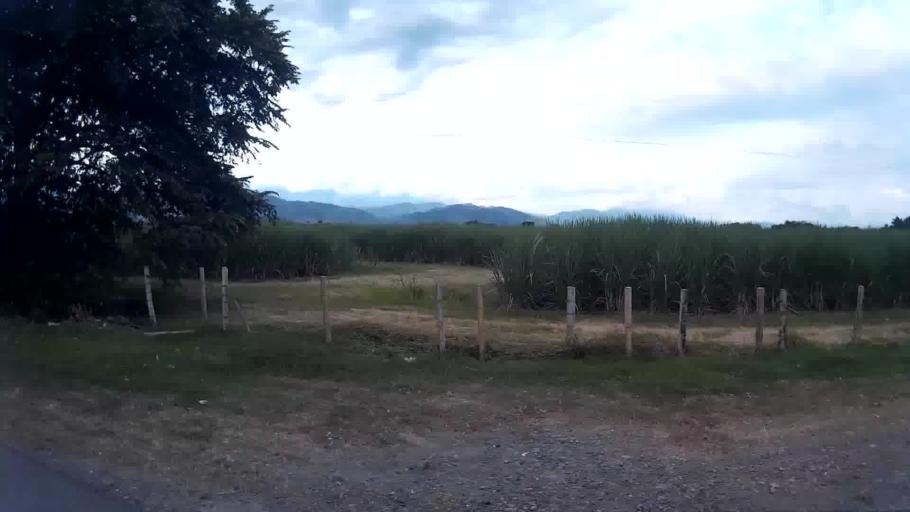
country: CO
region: Risaralda
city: La Virginia
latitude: 4.9088
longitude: -75.8756
